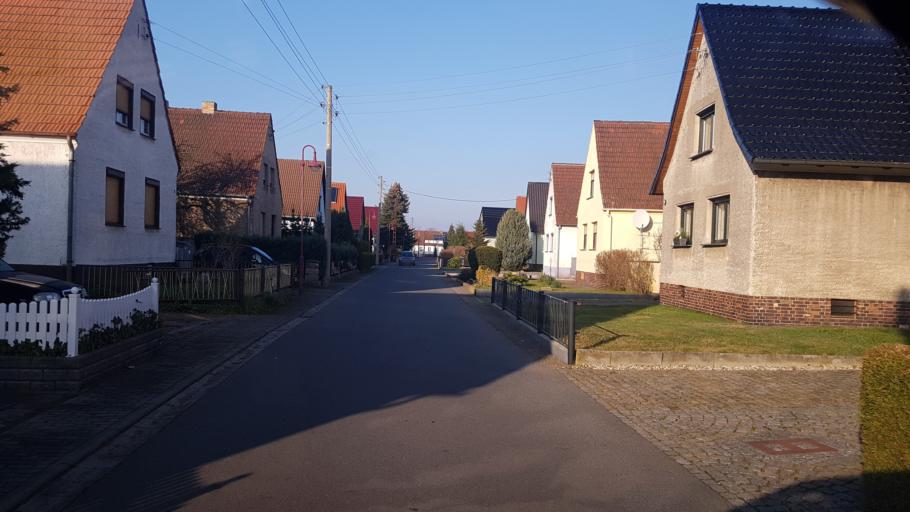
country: DE
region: Brandenburg
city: Lauchhammer
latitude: 51.4712
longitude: 13.7630
